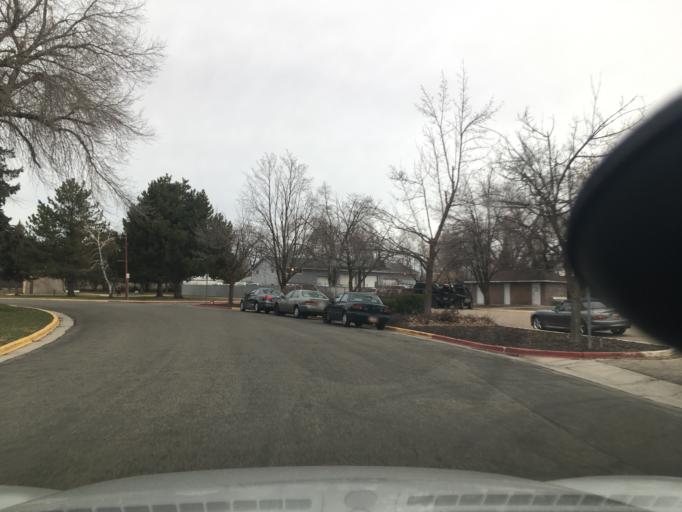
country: US
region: Utah
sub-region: Davis County
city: Layton
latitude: 41.0677
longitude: -111.9591
